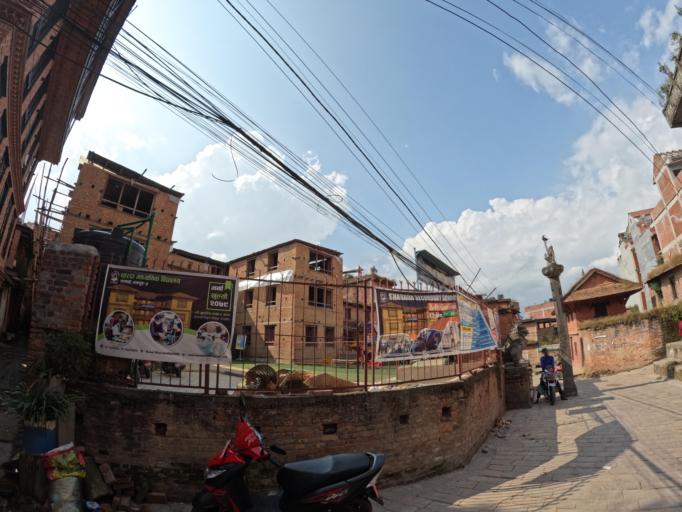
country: NP
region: Central Region
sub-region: Bagmati Zone
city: Bhaktapur
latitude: 27.6735
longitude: 85.4293
